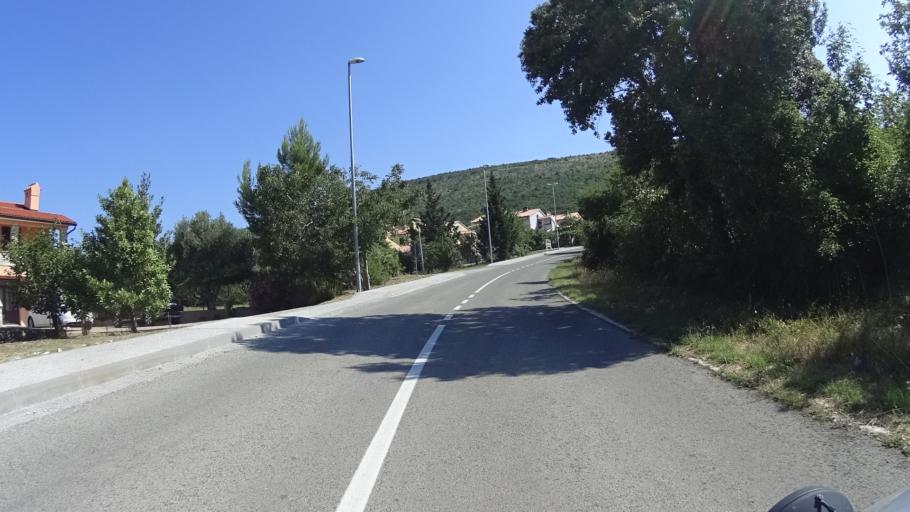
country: HR
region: Istarska
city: Rasa
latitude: 44.9829
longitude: 14.1124
